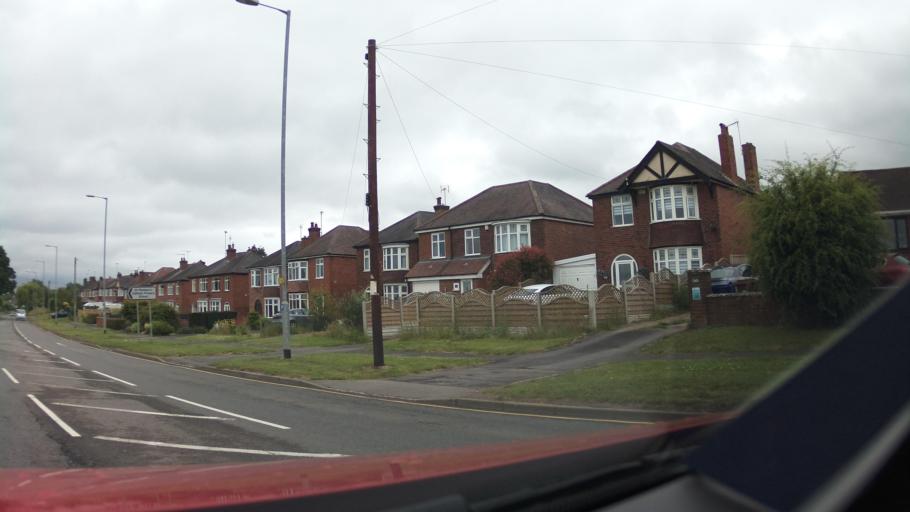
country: GB
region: England
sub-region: Staffordshire
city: Burton upon Trent
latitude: 52.8337
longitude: -1.6537
